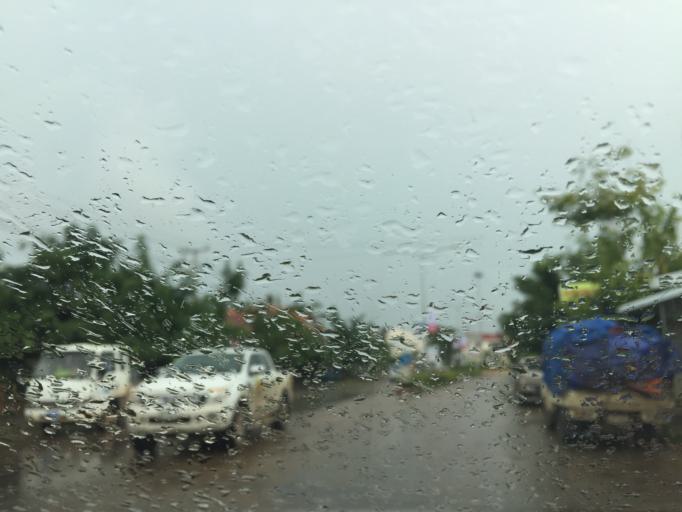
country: LA
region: Attapu
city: Attapu
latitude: 14.8215
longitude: 106.8123
